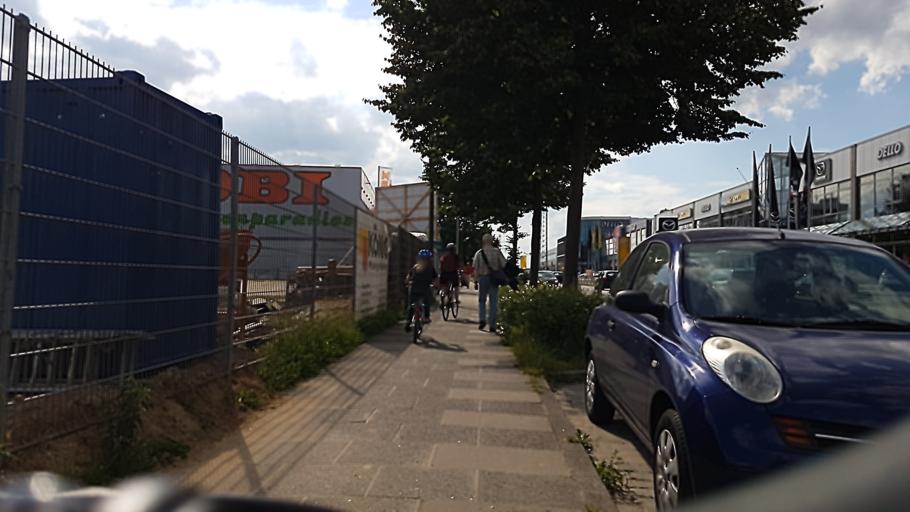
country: DE
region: Hamburg
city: Hamburg-Nord
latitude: 53.6012
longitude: 9.9808
